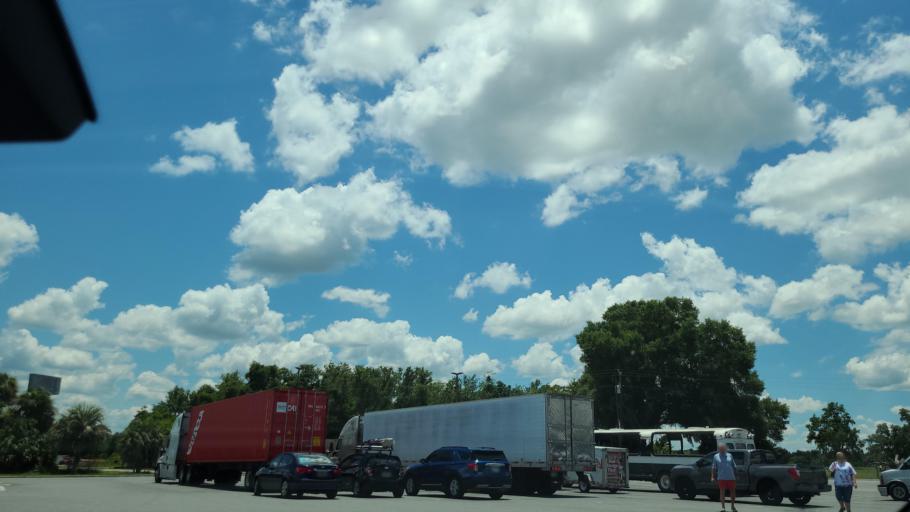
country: US
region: Florida
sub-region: Alachua County
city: High Springs
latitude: 29.9958
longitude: -82.5982
